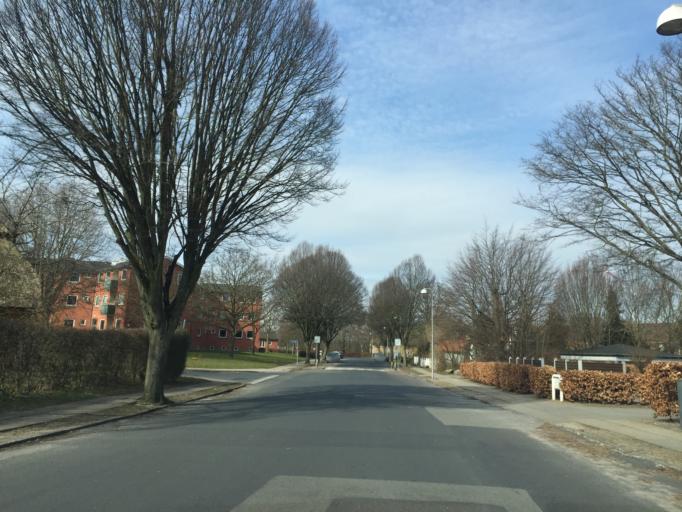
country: DK
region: South Denmark
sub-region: Odense Kommune
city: Seden
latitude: 55.3961
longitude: 10.4274
